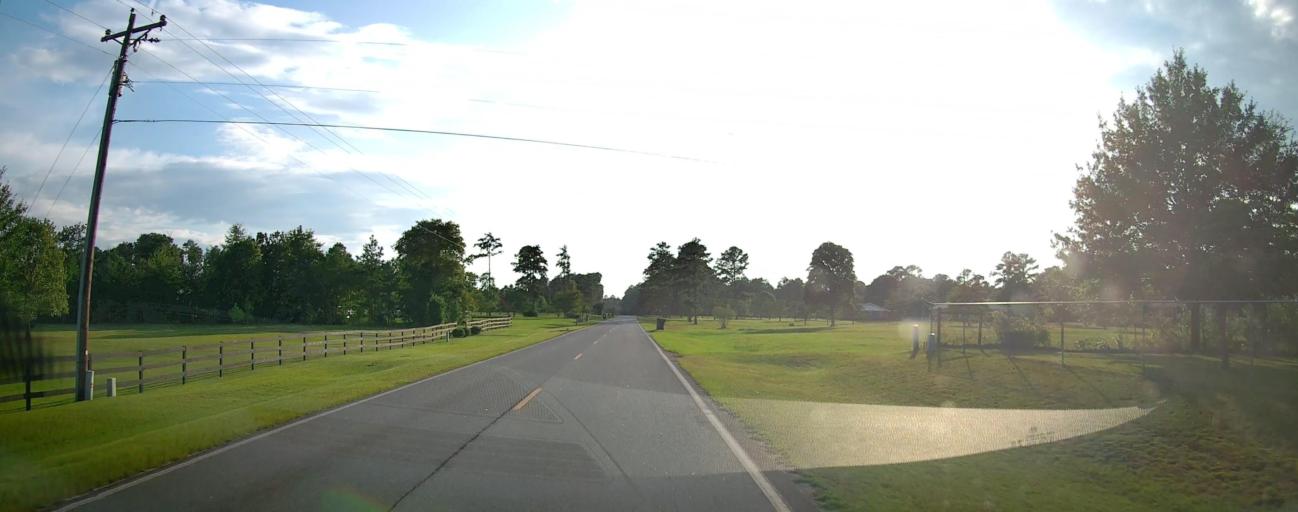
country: US
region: Georgia
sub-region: Peach County
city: Byron
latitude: 32.7054
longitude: -83.8106
